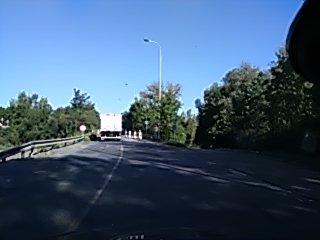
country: CZ
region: Pardubicky
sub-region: Okres Pardubice
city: Pardubice
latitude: 50.0355
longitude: 15.7495
